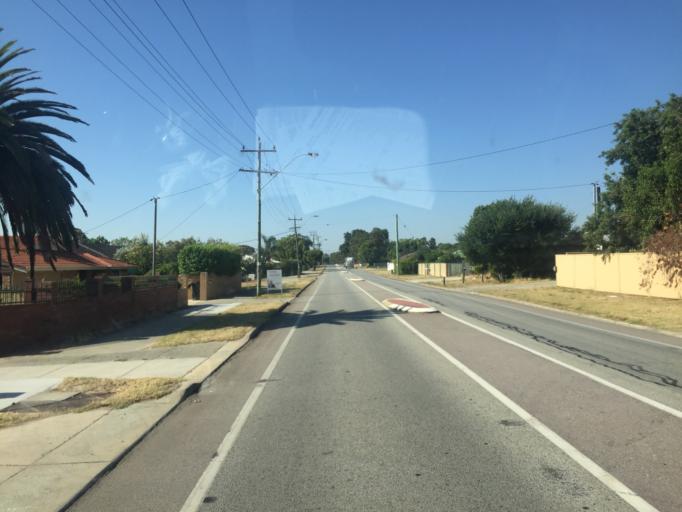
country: AU
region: Western Australia
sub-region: Gosnells
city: Maddington
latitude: -32.0389
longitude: 115.9820
